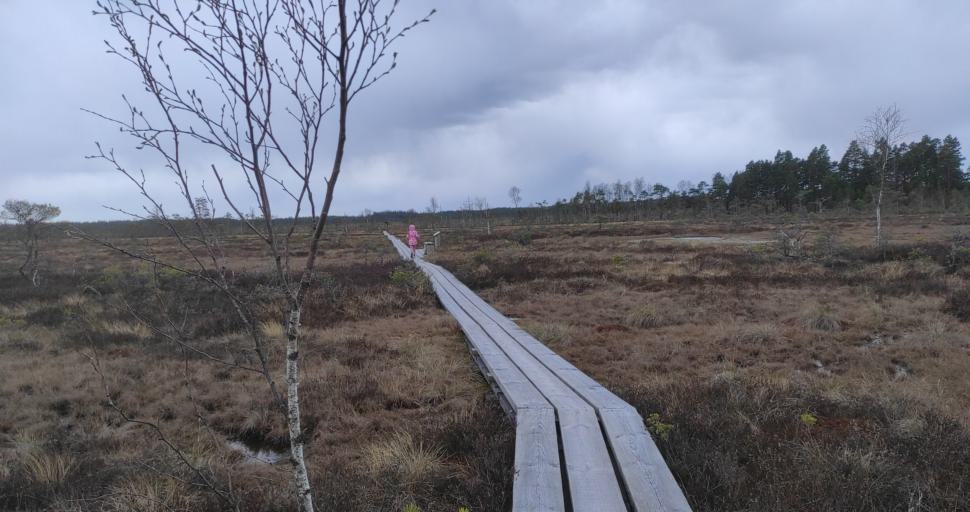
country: LV
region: Dundaga
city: Dundaga
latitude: 57.3460
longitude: 22.1566
